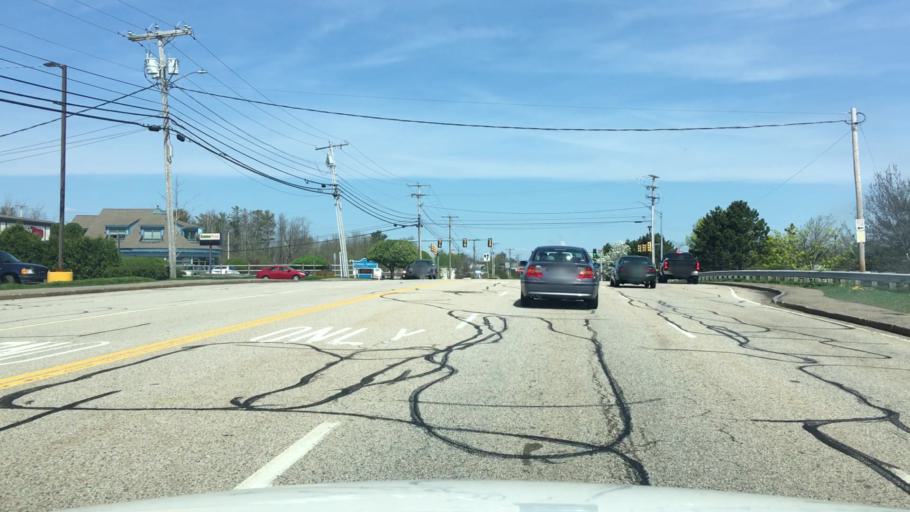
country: US
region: Maine
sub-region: York County
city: South Eliot
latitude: 43.0893
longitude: -70.7909
